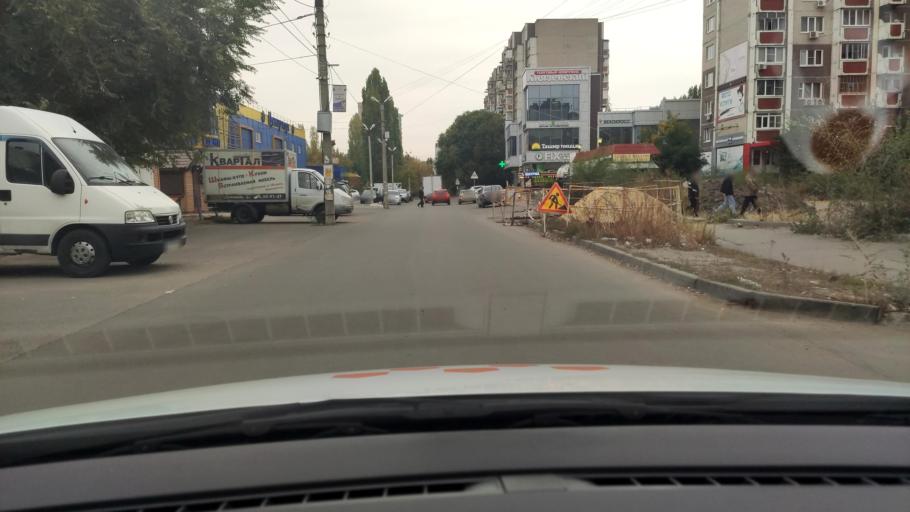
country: RU
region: Voronezj
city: Podgornoye
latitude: 51.7136
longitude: 39.1675
